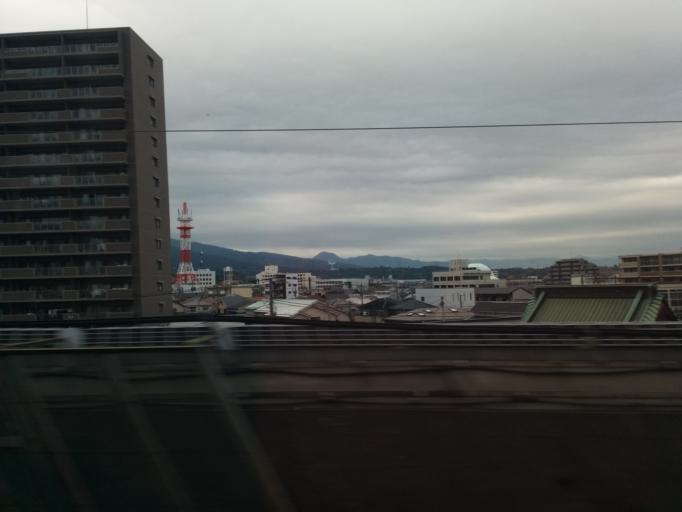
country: JP
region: Kanagawa
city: Odawara
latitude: 35.2615
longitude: 139.1593
